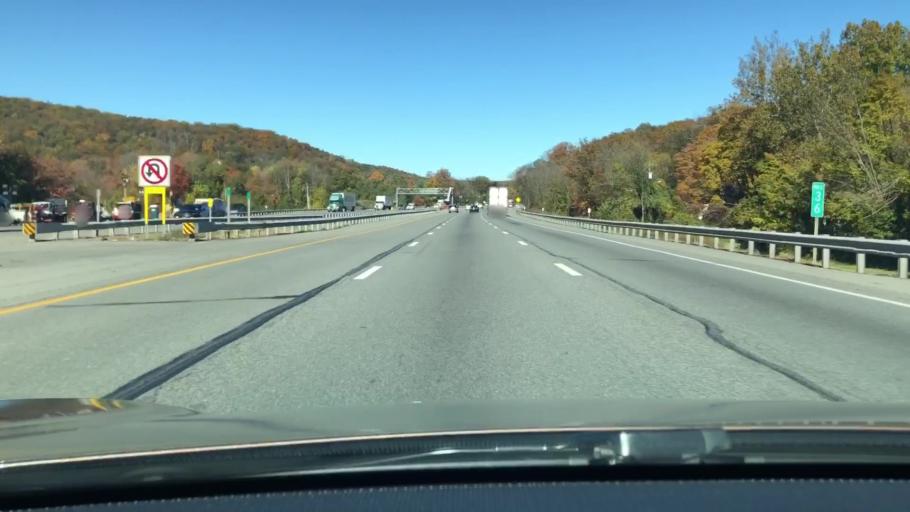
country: US
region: New York
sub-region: Rockland County
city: Sloatsburg
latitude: 41.1912
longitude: -74.1816
